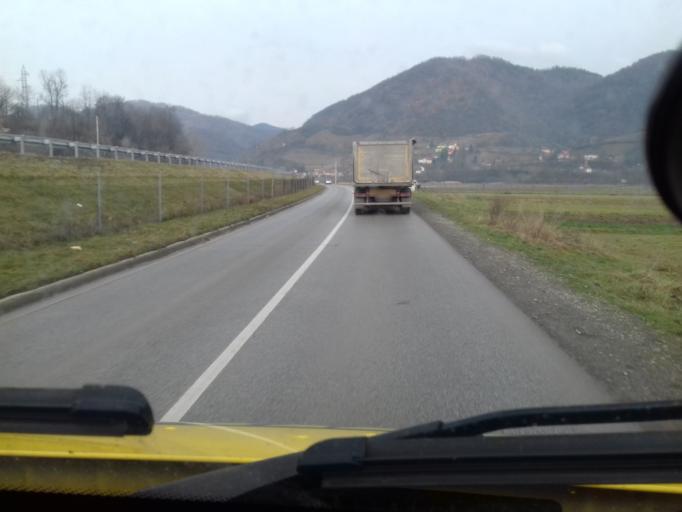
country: BA
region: Federation of Bosnia and Herzegovina
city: Dobrinje
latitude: 44.0424
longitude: 18.1210
